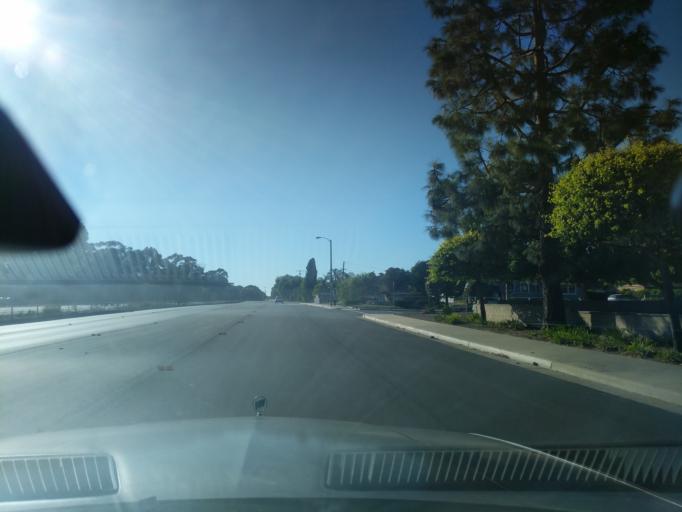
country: US
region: California
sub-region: Santa Barbara County
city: Goleta
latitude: 34.4396
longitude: -119.8361
